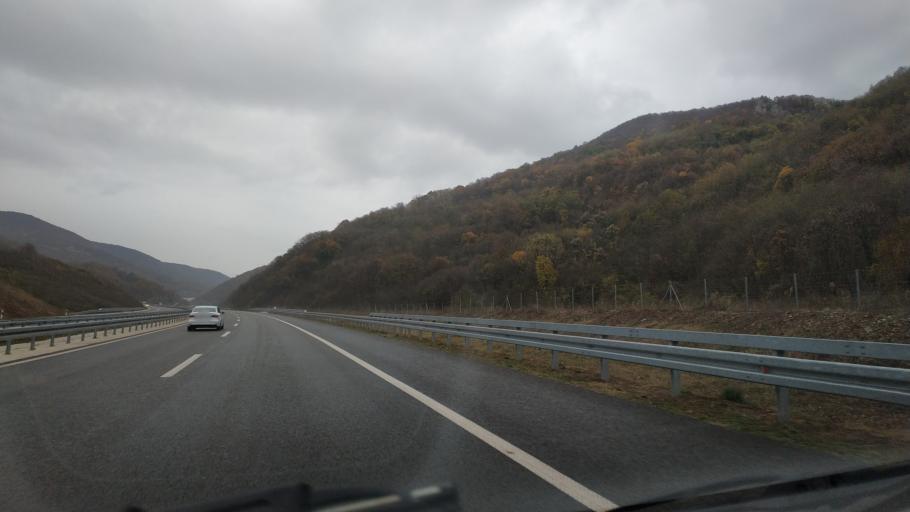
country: RS
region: Central Serbia
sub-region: Nisavski Okrug
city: Niska Banja
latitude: 43.2990
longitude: 22.0654
